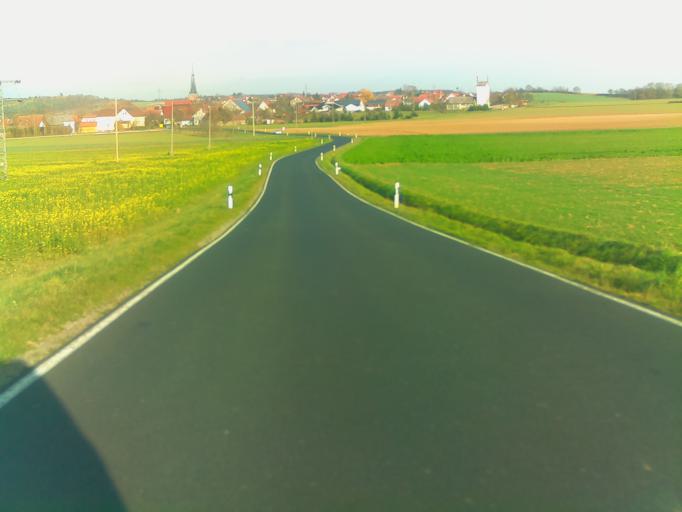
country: DE
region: Bavaria
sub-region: Regierungsbezirk Unterfranken
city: Neunkirchen
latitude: 49.7300
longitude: 9.4414
